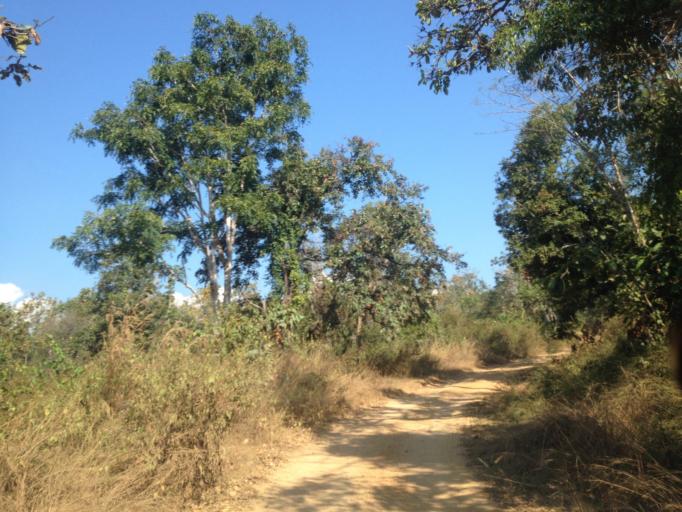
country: TH
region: Mae Hong Son
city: Ban Huai I Huak
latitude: 18.1156
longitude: 98.2078
